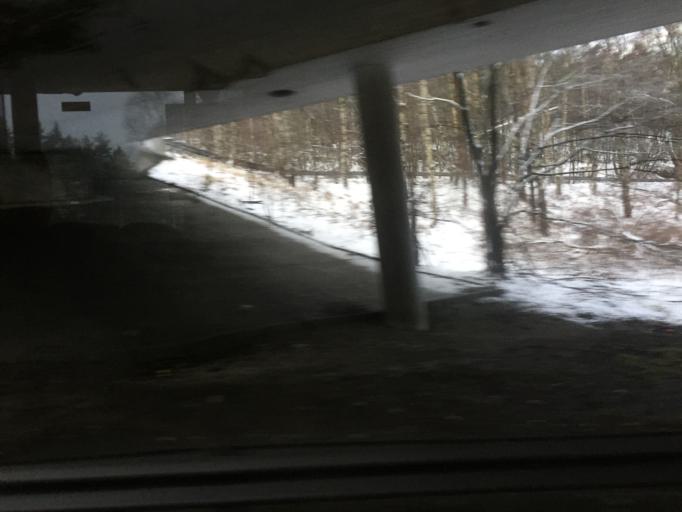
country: NO
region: Akershus
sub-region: Oppegard
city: Kolbotn
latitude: 59.8383
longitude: 10.7793
